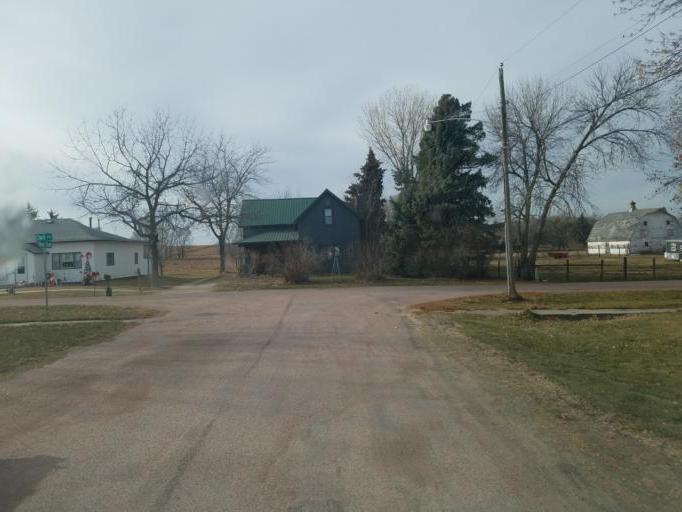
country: US
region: Nebraska
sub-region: Knox County
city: Creighton
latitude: 42.4599
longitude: -97.9087
